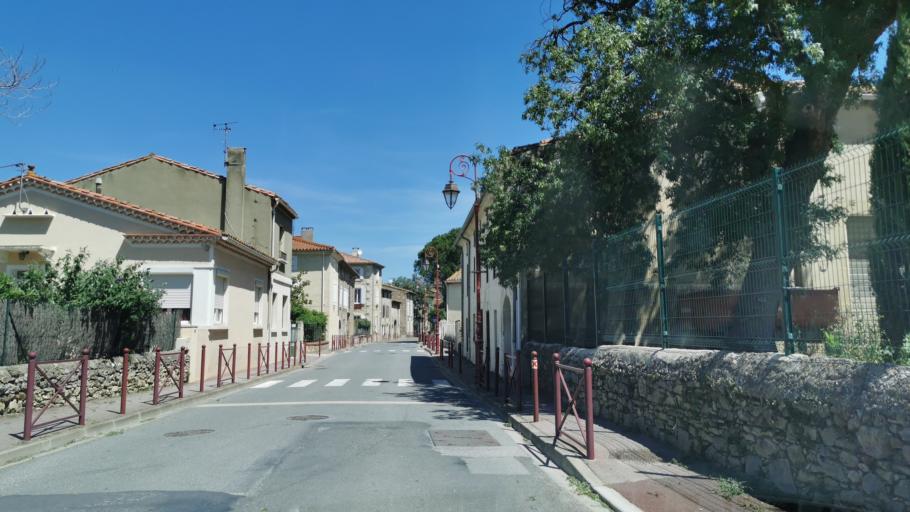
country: FR
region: Languedoc-Roussillon
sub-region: Departement de l'Aude
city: Canet
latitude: 43.2268
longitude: 2.8469
